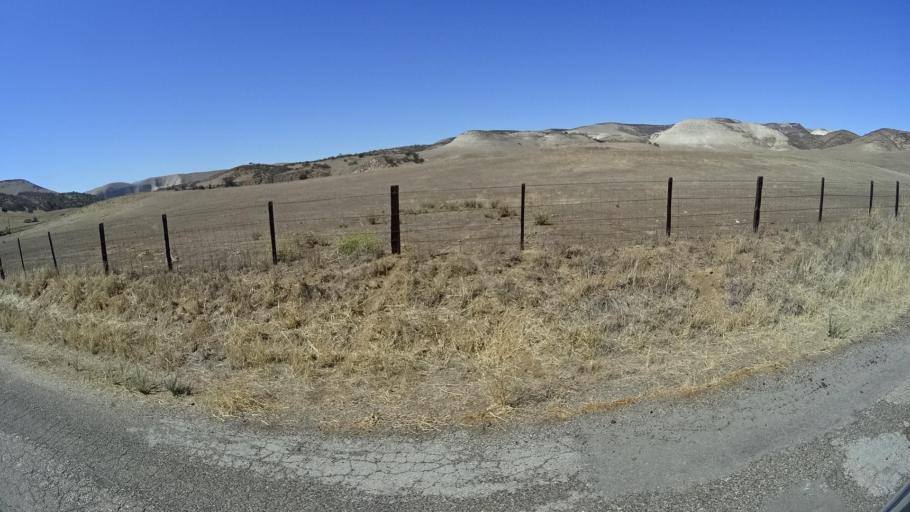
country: US
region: California
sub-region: Monterey County
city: King City
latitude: 36.2719
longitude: -120.9917
